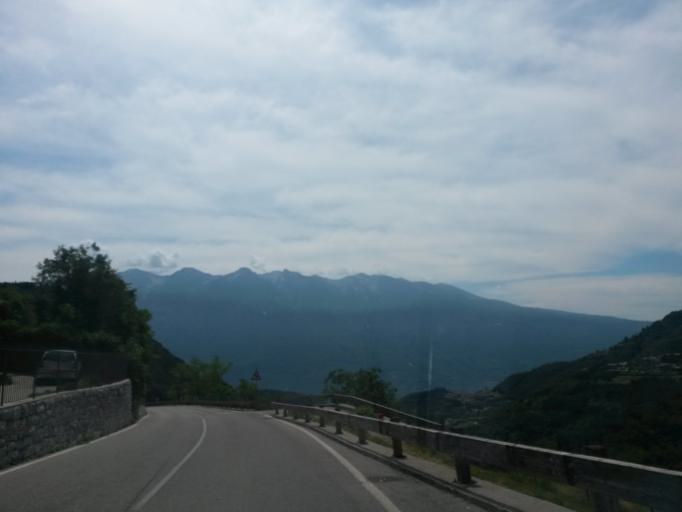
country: IT
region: Lombardy
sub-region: Provincia di Brescia
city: Pieve
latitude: 45.7901
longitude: 10.7484
